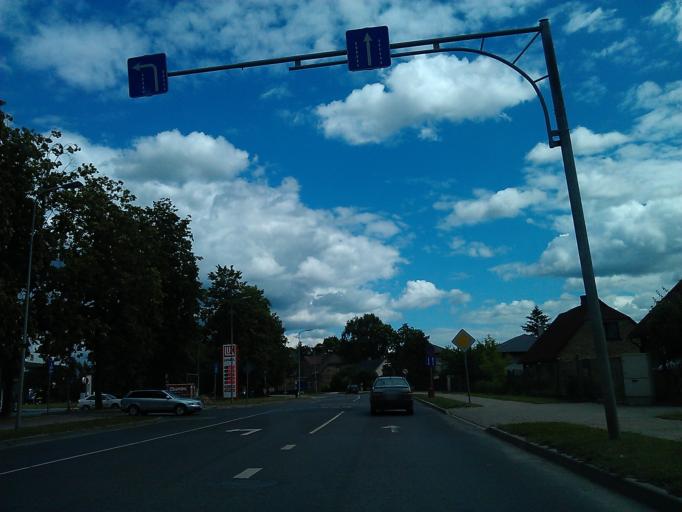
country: LV
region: Jelgava
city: Jelgava
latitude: 56.6367
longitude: 23.7107
